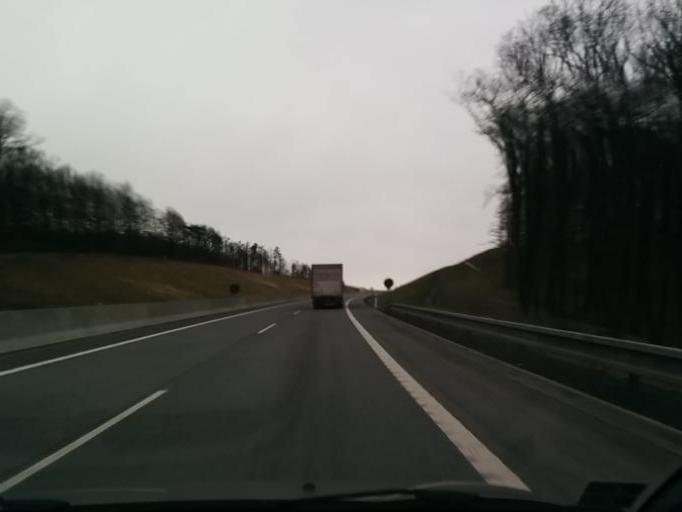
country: SK
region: Nitriansky
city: Tlmace
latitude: 48.3725
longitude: 18.5142
